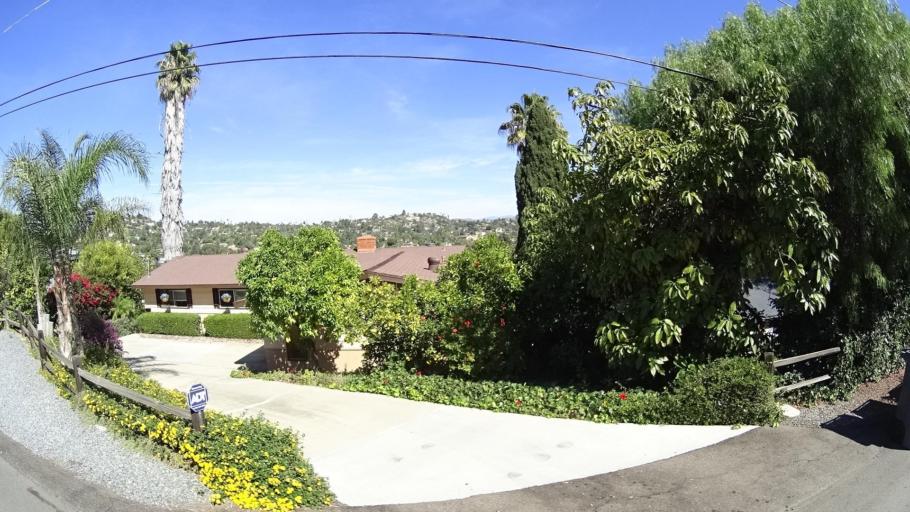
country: US
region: California
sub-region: San Diego County
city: Casa de Oro-Mount Helix
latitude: 32.7496
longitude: -116.9680
